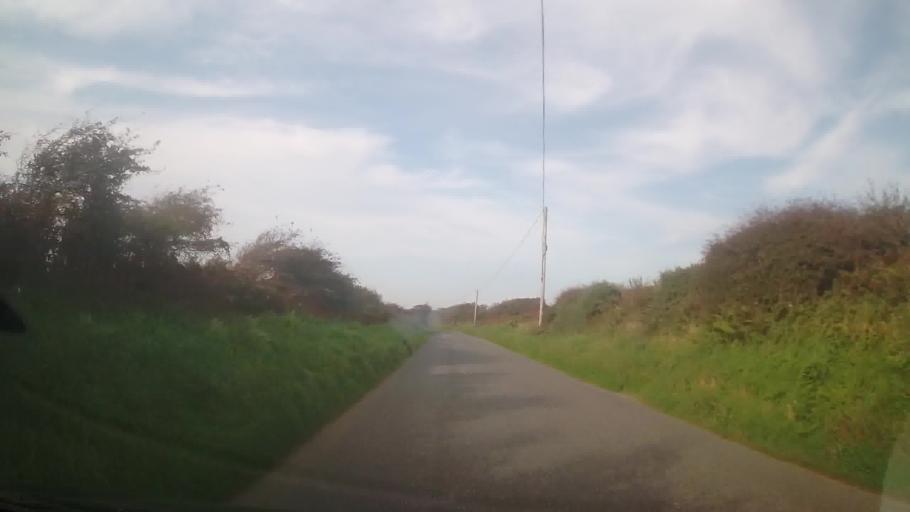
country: GB
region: Wales
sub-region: Pembrokeshire
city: Camrose
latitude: 51.8670
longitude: -5.0508
